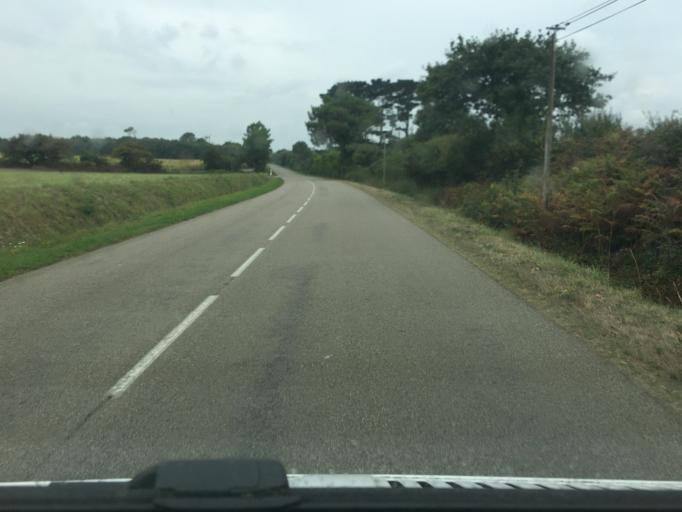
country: FR
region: Brittany
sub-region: Departement du Finistere
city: Poullan-sur-Mer
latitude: 48.0809
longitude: -4.4364
